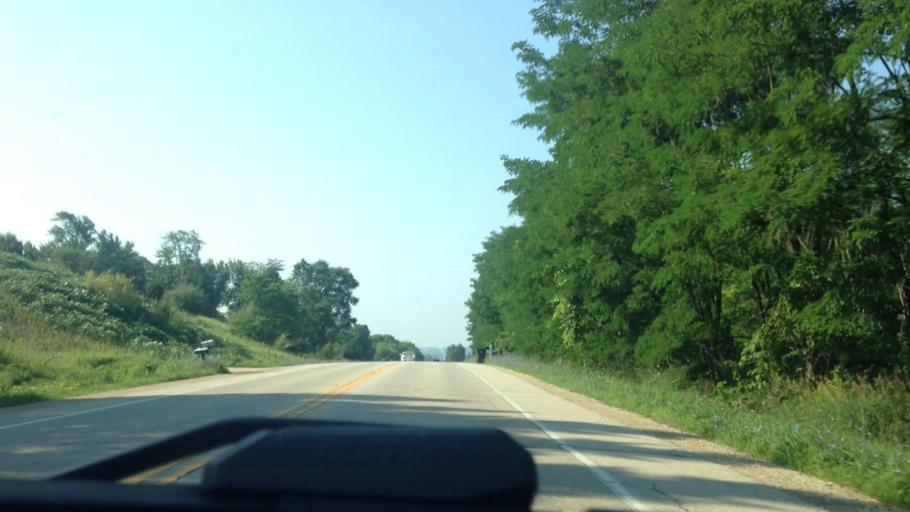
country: US
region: Wisconsin
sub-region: Washington County
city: Slinger
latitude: 43.3036
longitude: -88.2608
